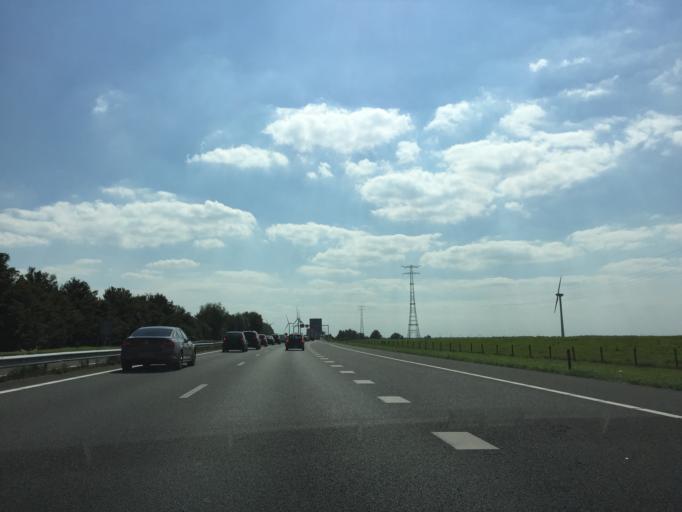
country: NL
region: North Brabant
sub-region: Gemeente Moerdijk
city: Willemstad
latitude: 51.7302
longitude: 4.4095
